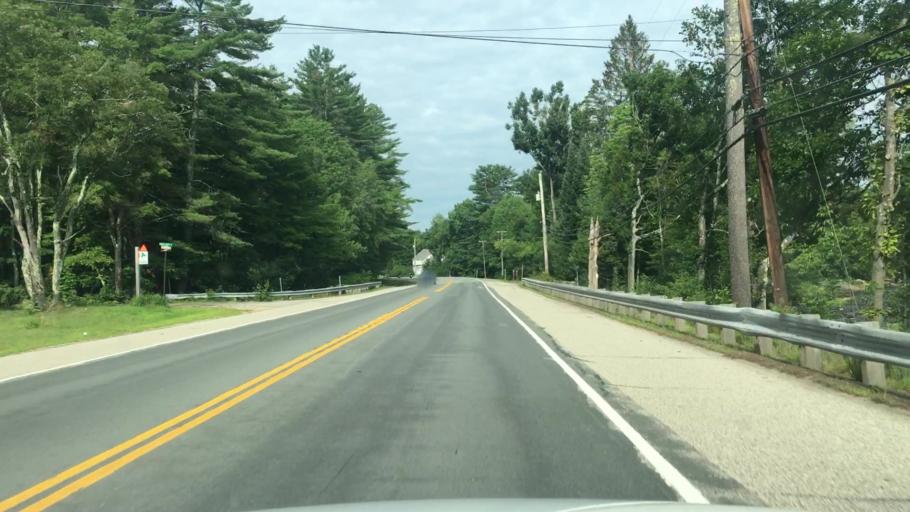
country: US
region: New Hampshire
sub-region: Carroll County
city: Tamworth
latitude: 43.8298
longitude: -71.2870
